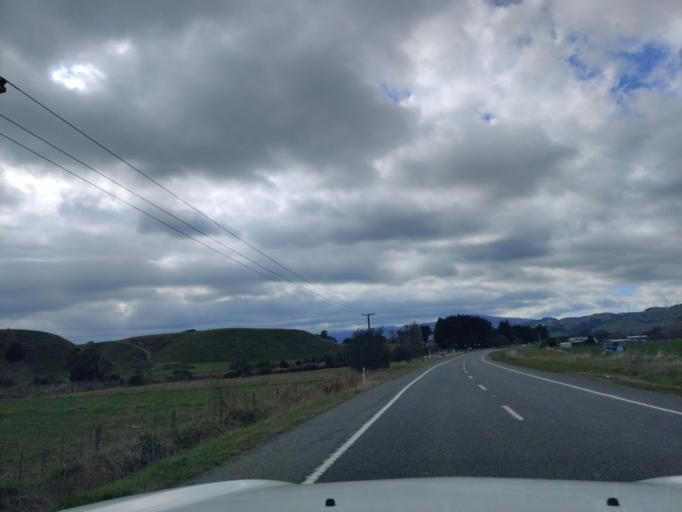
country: NZ
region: Manawatu-Wanganui
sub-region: Palmerston North City
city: Palmerston North
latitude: -40.3015
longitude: 175.7346
